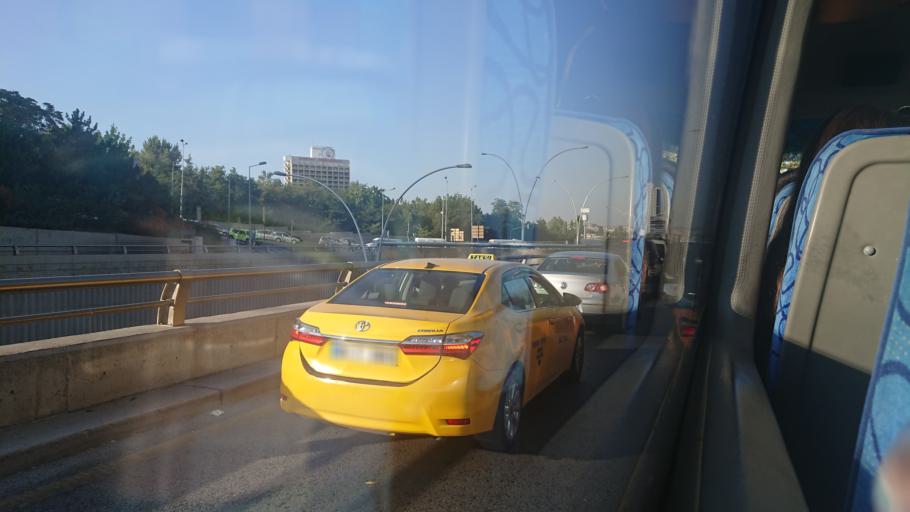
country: TR
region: Ankara
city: Ankara
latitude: 39.9306
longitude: 32.8189
